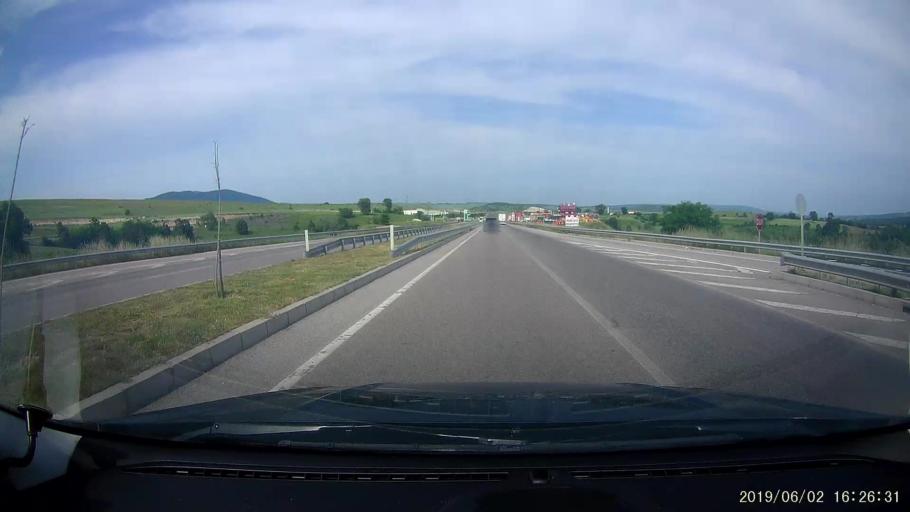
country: TR
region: Samsun
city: Ladik
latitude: 41.0001
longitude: 35.8044
